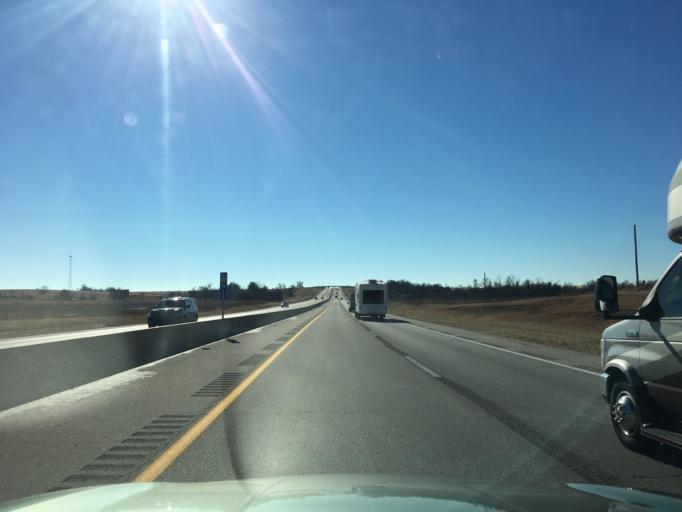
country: US
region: Oklahoma
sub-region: Kay County
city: Blackwell
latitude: 37.0107
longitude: -97.3391
